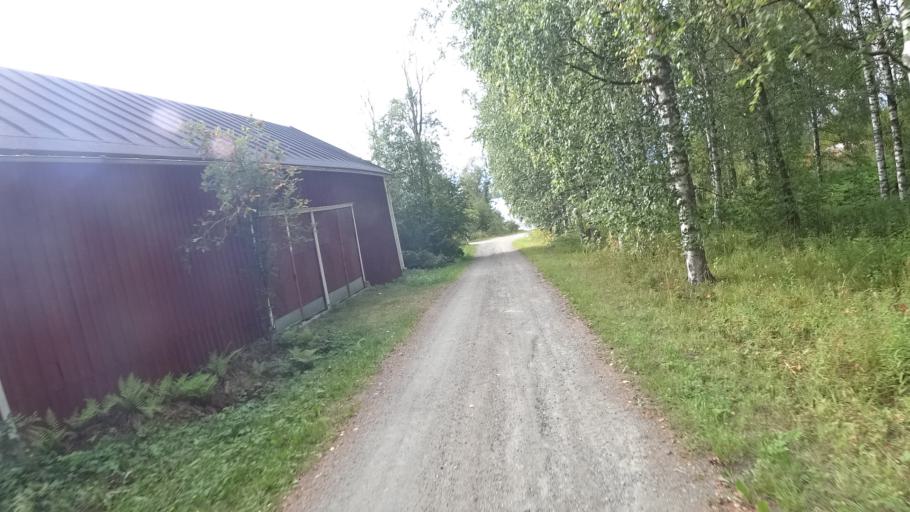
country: FI
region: North Karelia
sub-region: Joensuu
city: Ilomantsi
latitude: 62.6764
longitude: 30.9128
